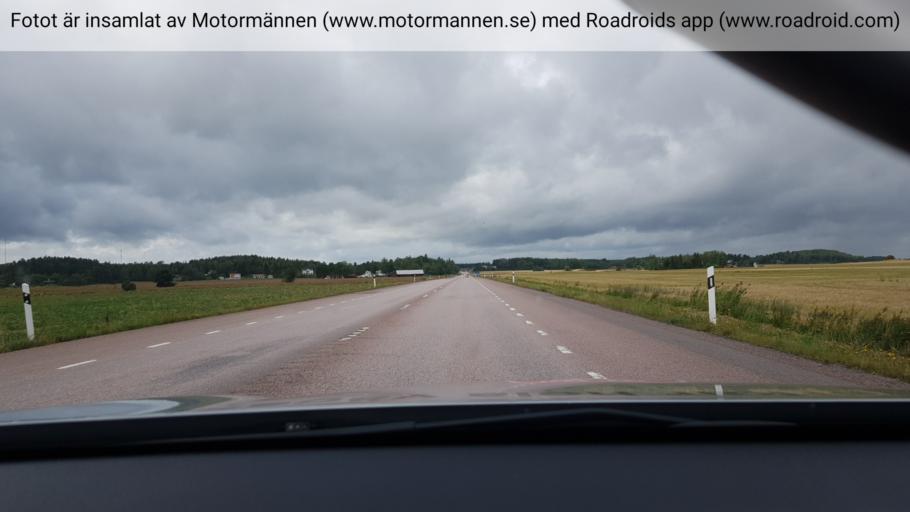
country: SE
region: Uppsala
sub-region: Knivsta Kommun
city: Knivsta
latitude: 59.7491
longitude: 17.9260
